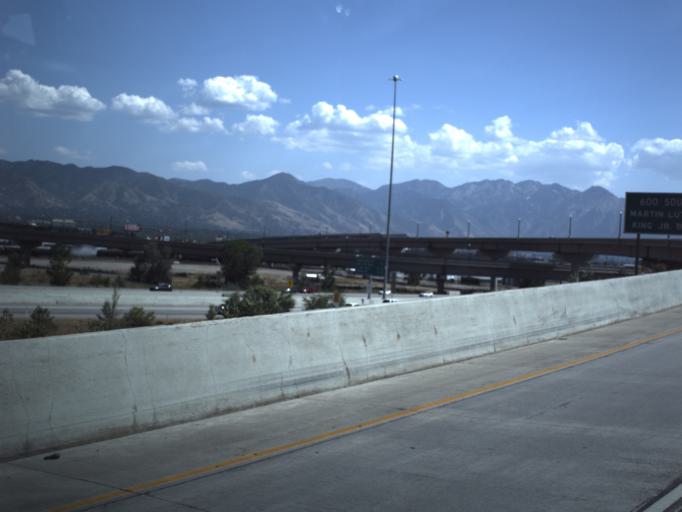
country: US
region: Utah
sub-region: Salt Lake County
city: Salt Lake City
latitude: 40.7581
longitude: -111.9148
